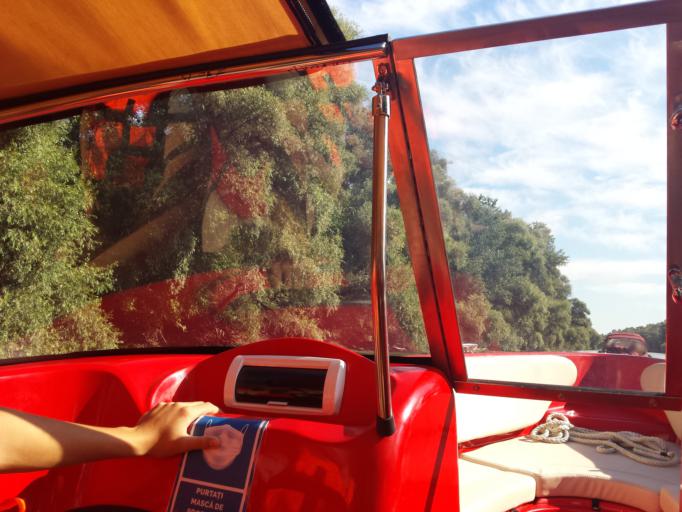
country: RO
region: Tulcea
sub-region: Comuna Nufaru
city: Nufaru
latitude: 45.2185
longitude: 28.8752
